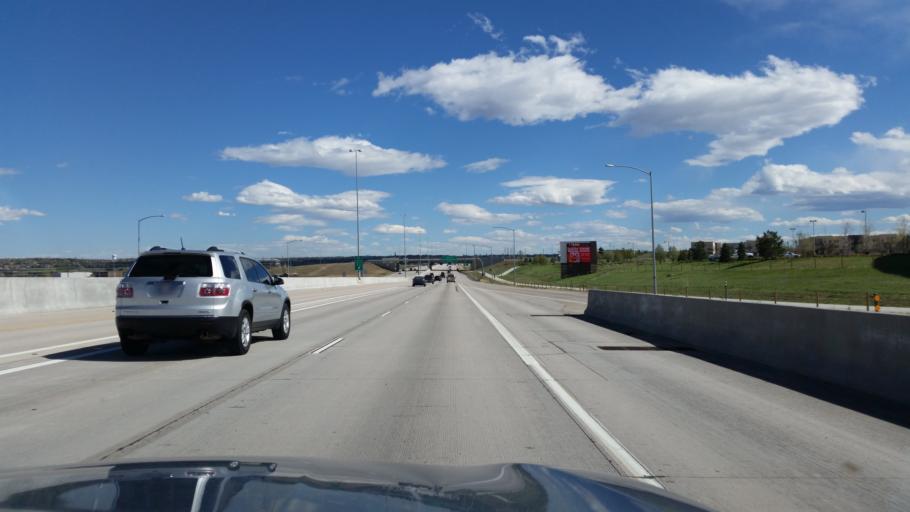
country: US
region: Colorado
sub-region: Broomfield County
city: Broomfield
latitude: 39.9059
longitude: -105.0848
